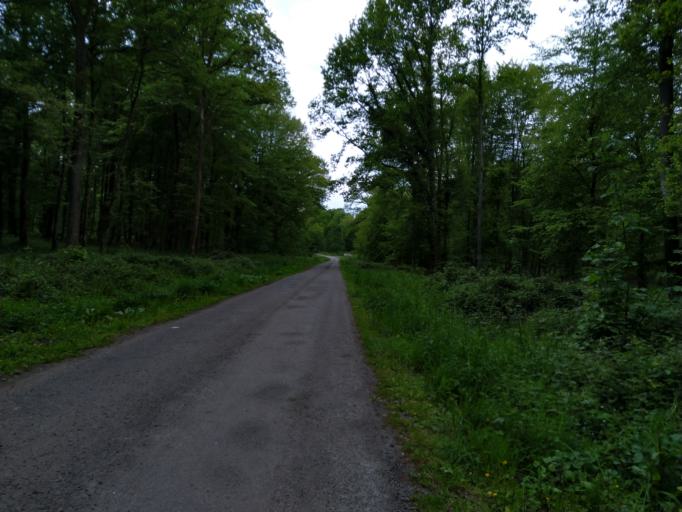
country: FR
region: Nord-Pas-de-Calais
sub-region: Departement du Nord
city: Gommegnies
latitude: 50.2199
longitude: 3.7054
